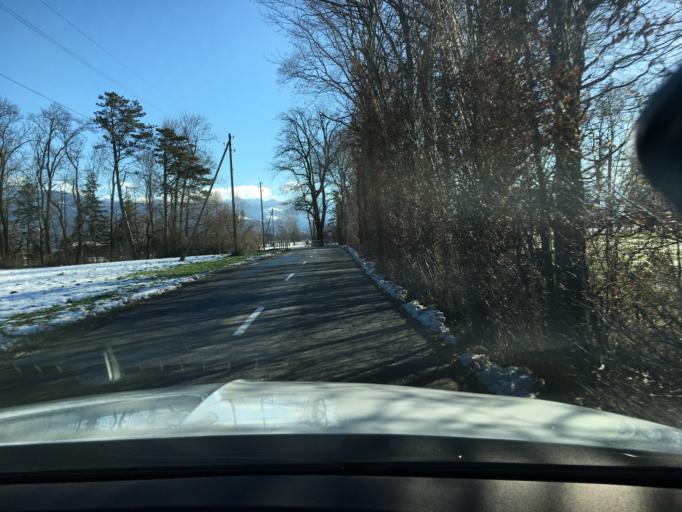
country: CH
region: Saint Gallen
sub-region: Wahlkreis Rheintal
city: Rebstein
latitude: 47.3789
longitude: 9.5872
